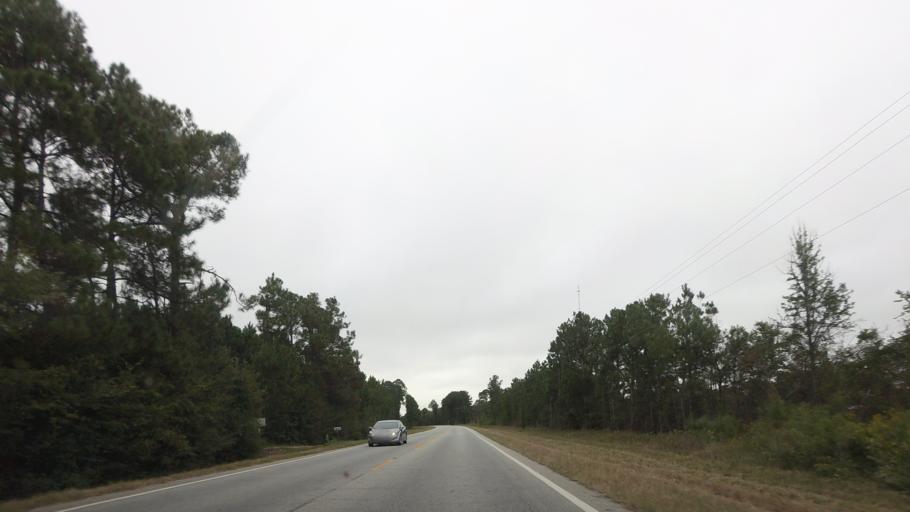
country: US
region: Georgia
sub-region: Berrien County
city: Ray City
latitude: 31.1415
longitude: -83.2171
